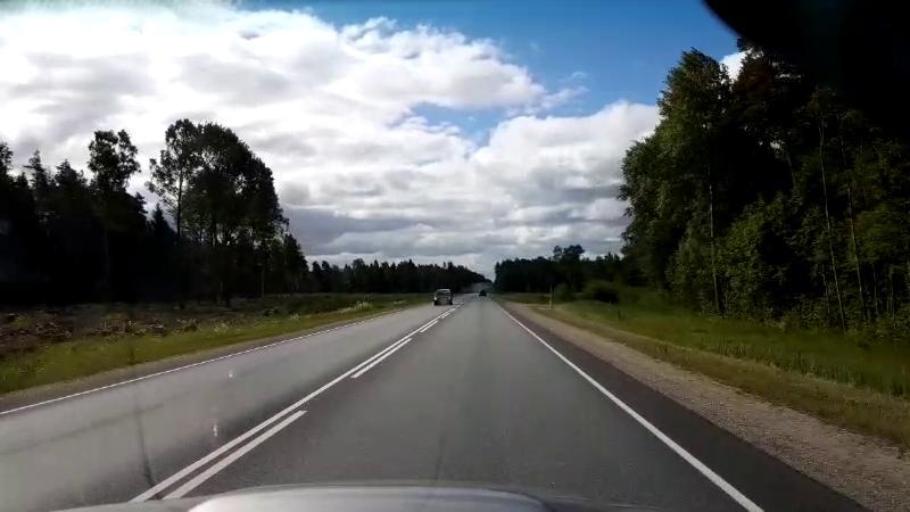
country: EE
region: Raplamaa
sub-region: Maerjamaa vald
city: Marjamaa
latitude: 59.0269
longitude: 24.4471
